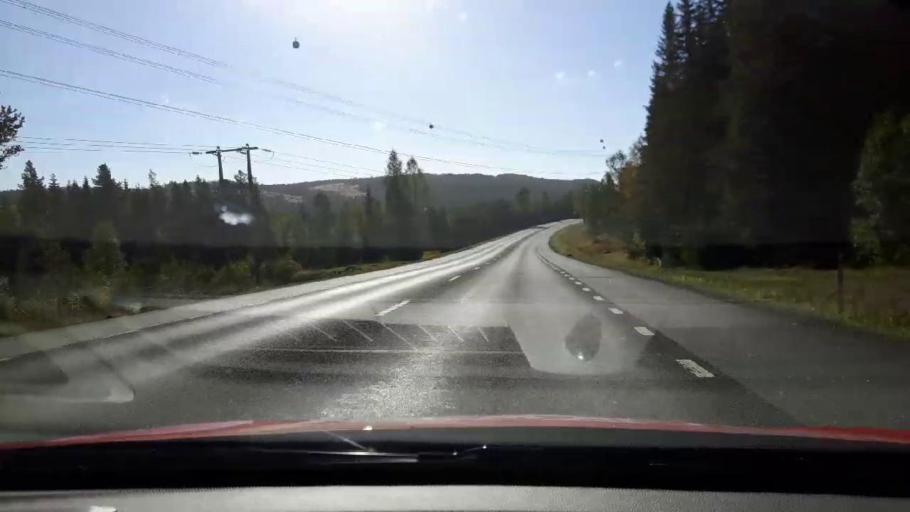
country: SE
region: Vaesternorrland
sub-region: Ange Kommun
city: Ange
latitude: 62.6753
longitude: 15.5985
